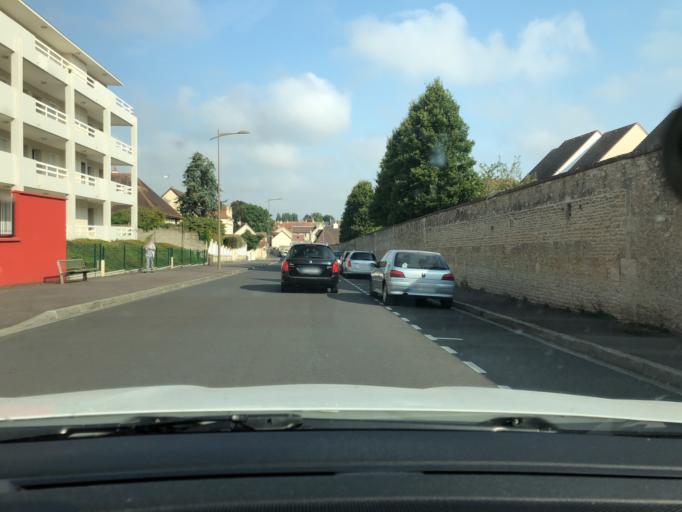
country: FR
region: Lower Normandy
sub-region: Departement du Calvados
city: Douvres-la-Delivrande
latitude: 49.2956
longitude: -0.3730
